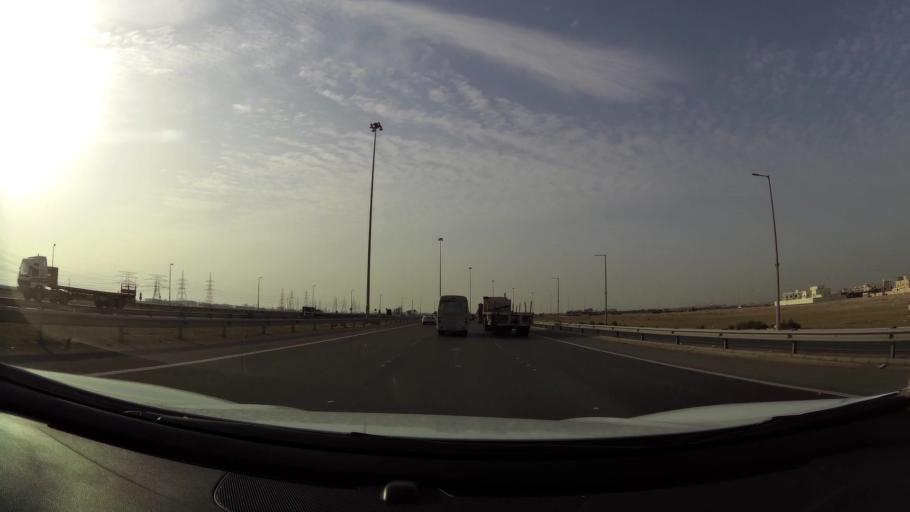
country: AE
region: Abu Dhabi
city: Abu Dhabi
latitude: 24.3061
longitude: 54.5314
